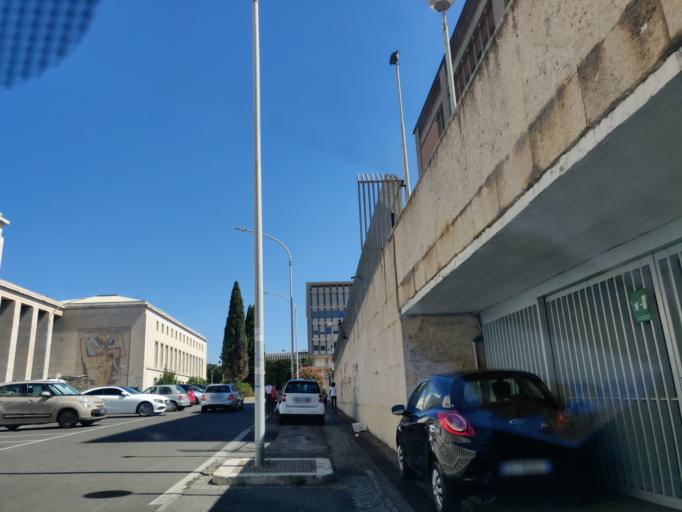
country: IT
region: Latium
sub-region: Citta metropolitana di Roma Capitale
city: Selcetta
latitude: 41.8320
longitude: 12.4726
